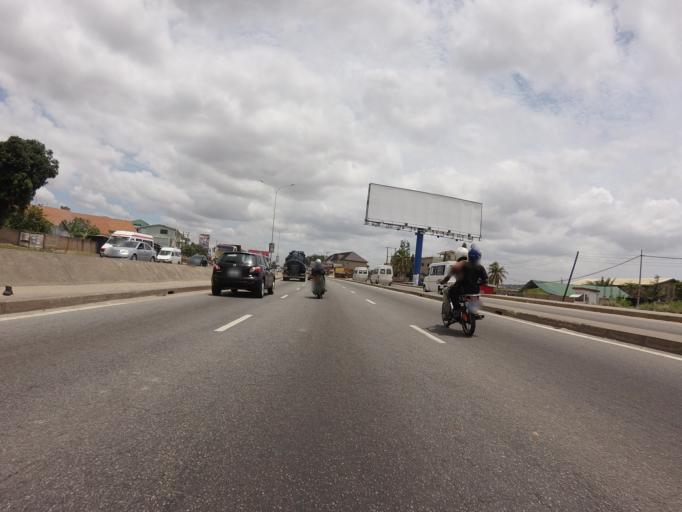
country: GH
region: Greater Accra
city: Gbawe
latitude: 5.5610
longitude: -0.2911
